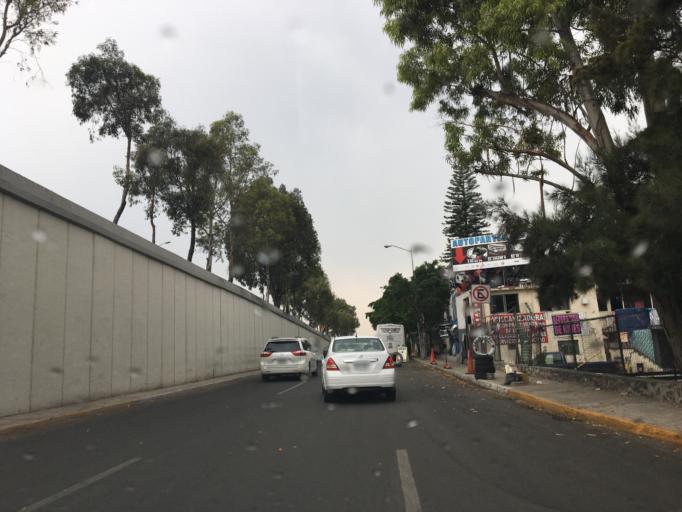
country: MX
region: Queretaro
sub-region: Queretaro
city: Santiago de Queretaro
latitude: 20.5797
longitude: -100.3744
